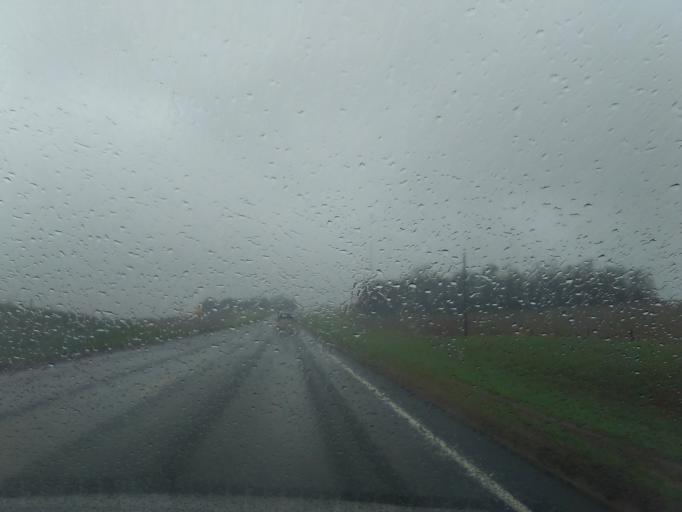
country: US
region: Nebraska
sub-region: Wayne County
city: Wayne
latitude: 42.1953
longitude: -97.1737
